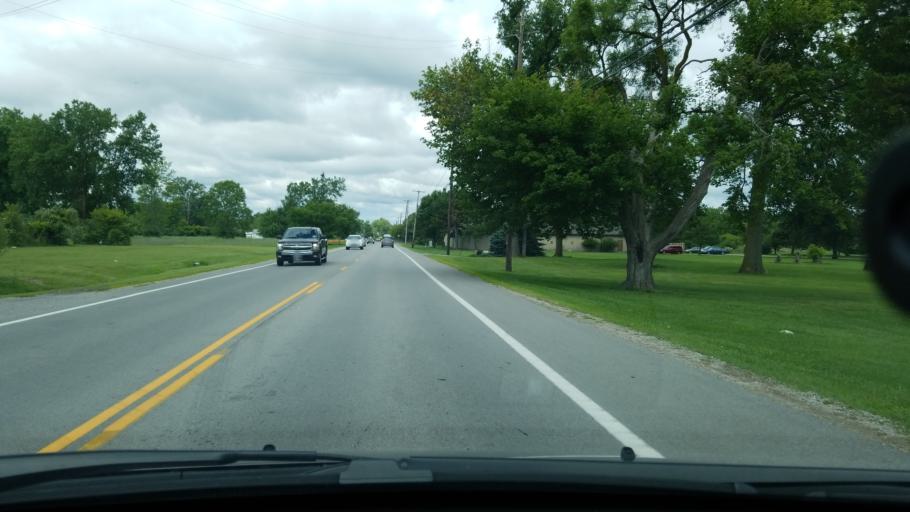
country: US
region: Ohio
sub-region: Erie County
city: Huron
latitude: 41.4074
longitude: -82.5992
